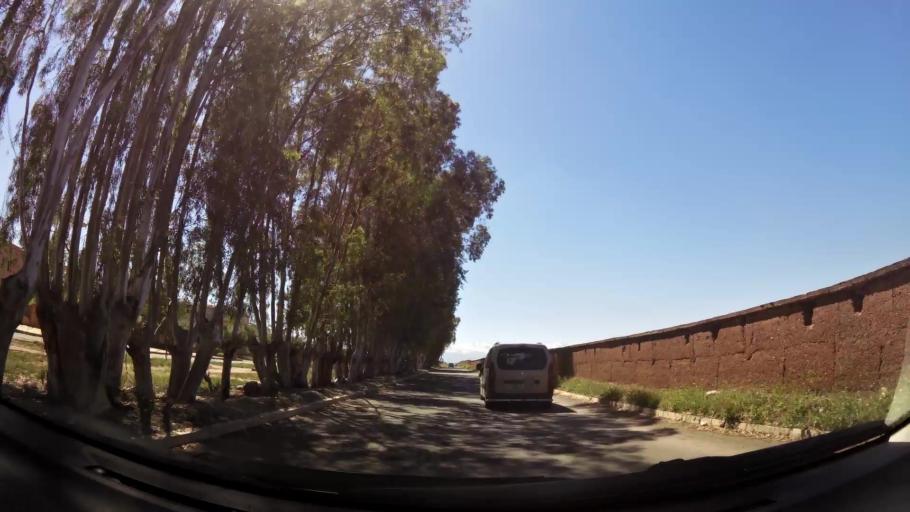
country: MA
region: Marrakech-Tensift-Al Haouz
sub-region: Marrakech
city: Marrakesh
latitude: 31.5872
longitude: -8.0061
